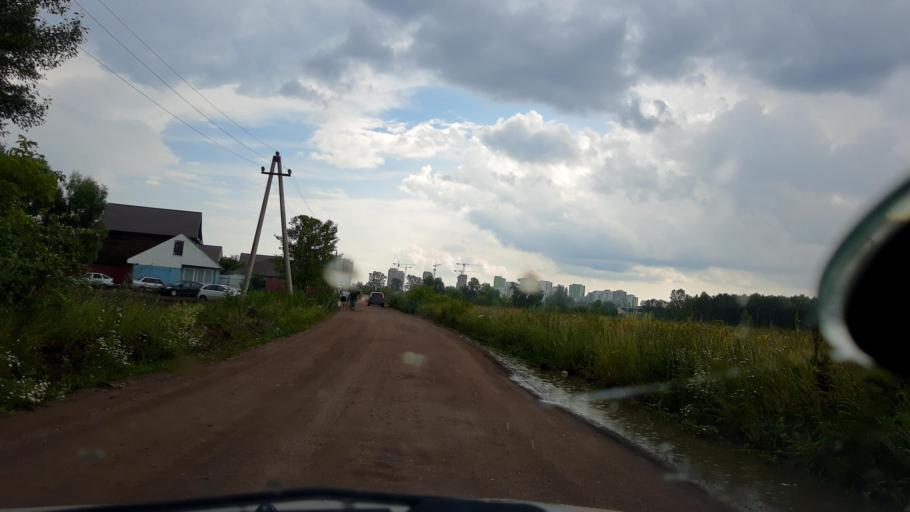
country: RU
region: Bashkortostan
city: Mikhaylovka
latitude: 54.7110
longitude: 55.8679
